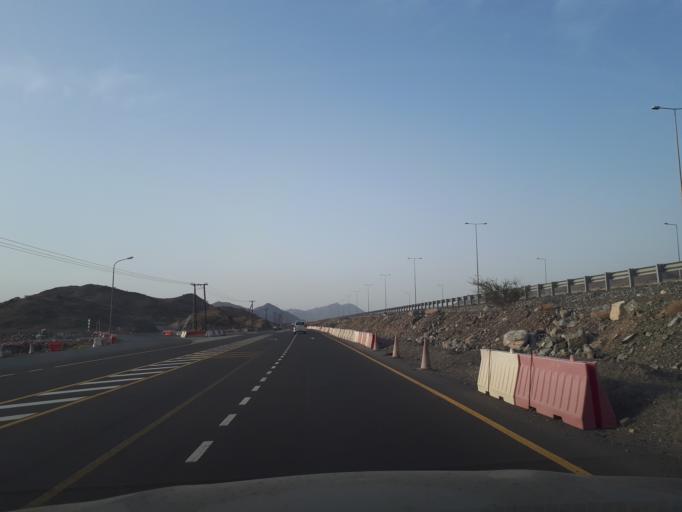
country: OM
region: Muhafazat ad Dakhiliyah
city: Sufalat Sama'il
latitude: 23.2826
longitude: 58.1078
